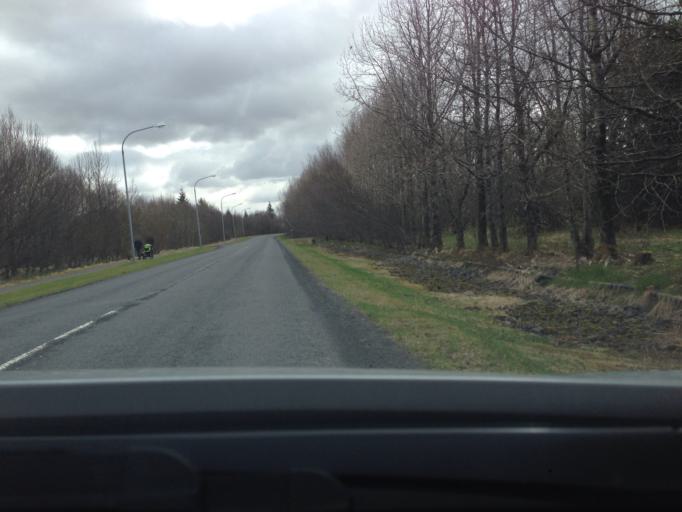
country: IS
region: South
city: Selfoss
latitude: 64.1185
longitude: -20.5017
